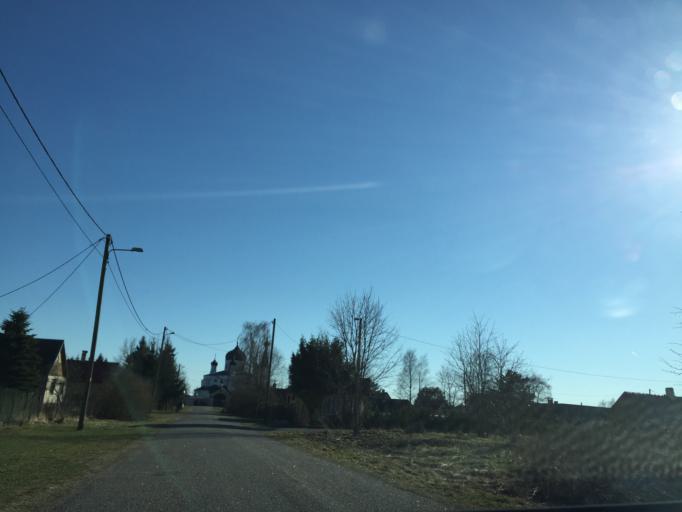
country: RU
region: Pskov
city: Gdov
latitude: 58.9996
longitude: 27.7391
